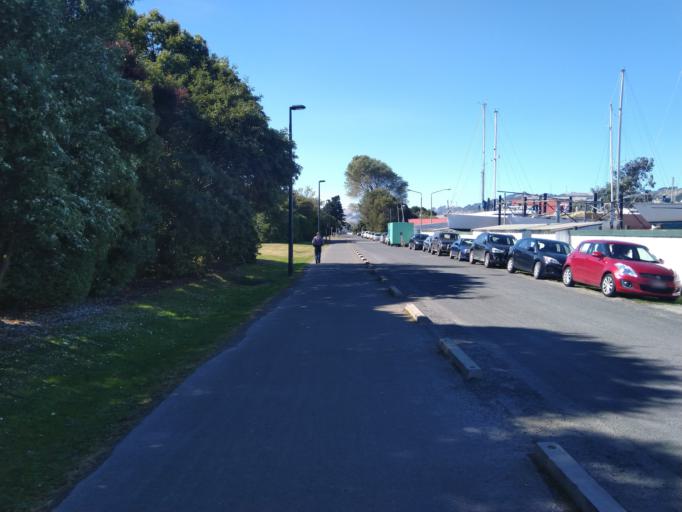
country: NZ
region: Otago
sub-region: Dunedin City
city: Dunedin
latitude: -45.8711
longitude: 170.5263
